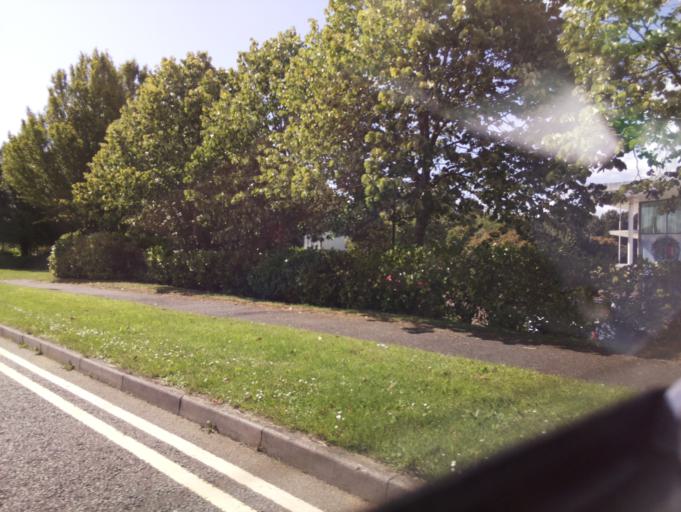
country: GB
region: England
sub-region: Milton Keynes
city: Loughton
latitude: 52.0228
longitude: -0.7725
